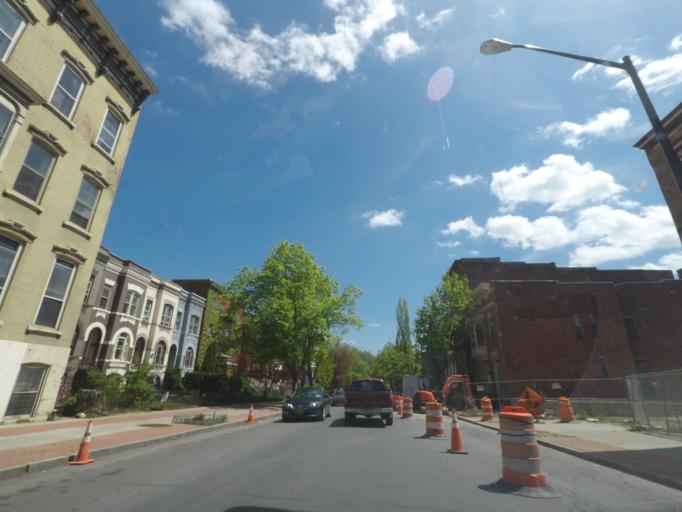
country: US
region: New York
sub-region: Albany County
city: Albany
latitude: 42.6511
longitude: -73.7653
